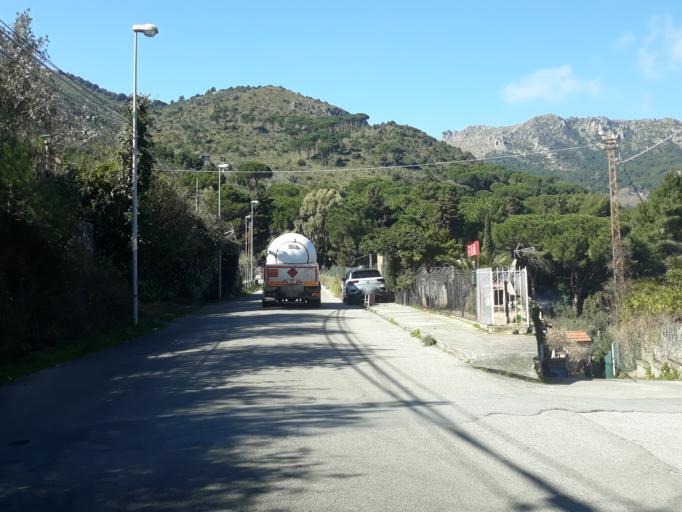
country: IT
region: Sicily
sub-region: Palermo
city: Piano dei Geli
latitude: 38.0857
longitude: 13.2607
